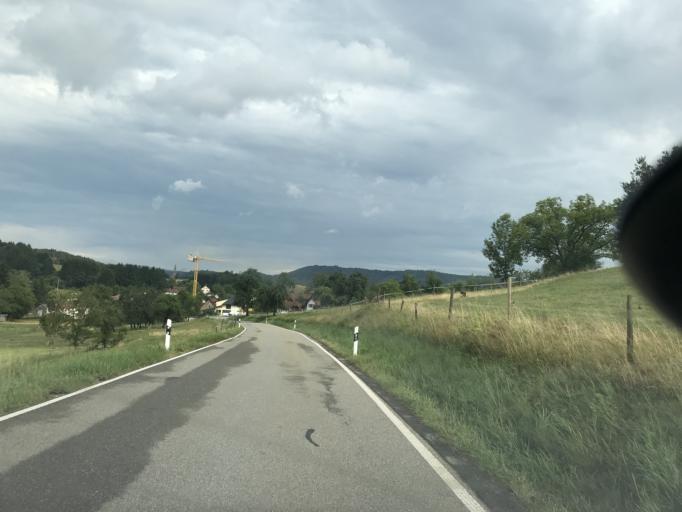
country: DE
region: Baden-Wuerttemberg
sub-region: Freiburg Region
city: Steinen
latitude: 47.6922
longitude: 7.7323
